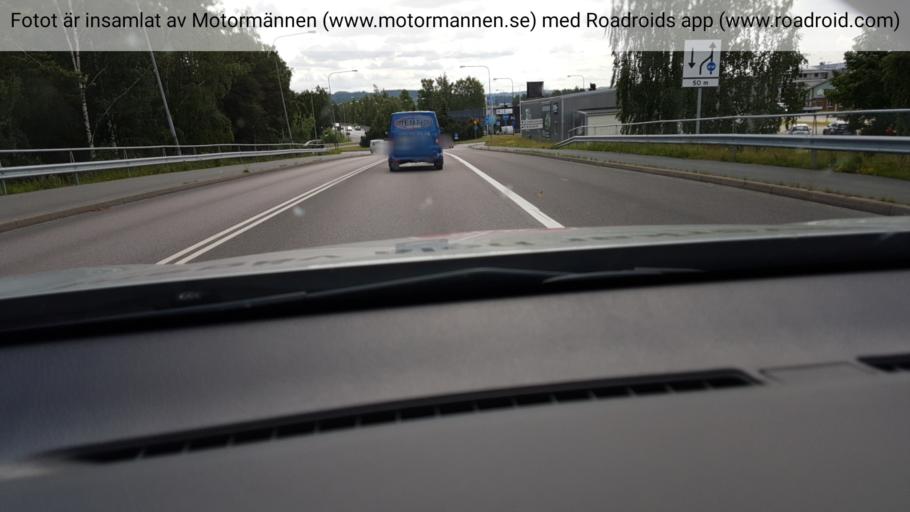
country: SE
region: Joenkoeping
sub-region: Jonkopings Kommun
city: Jonkoping
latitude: 57.7629
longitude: 14.1679
